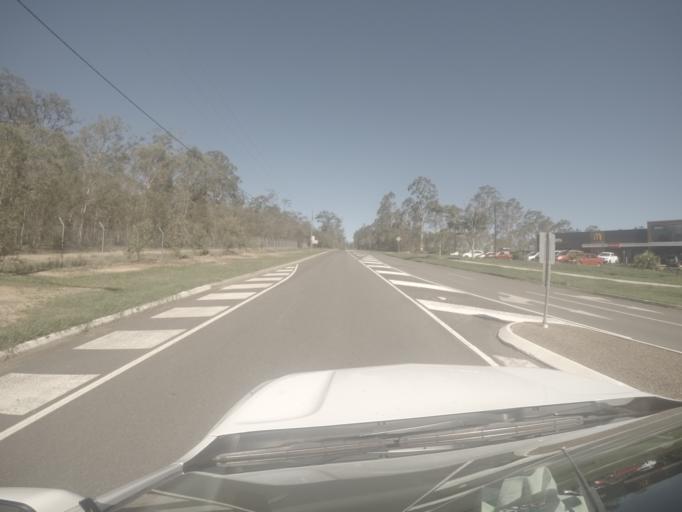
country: AU
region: Queensland
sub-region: Ipswich
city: Springfield
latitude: -27.6510
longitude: 152.9214
